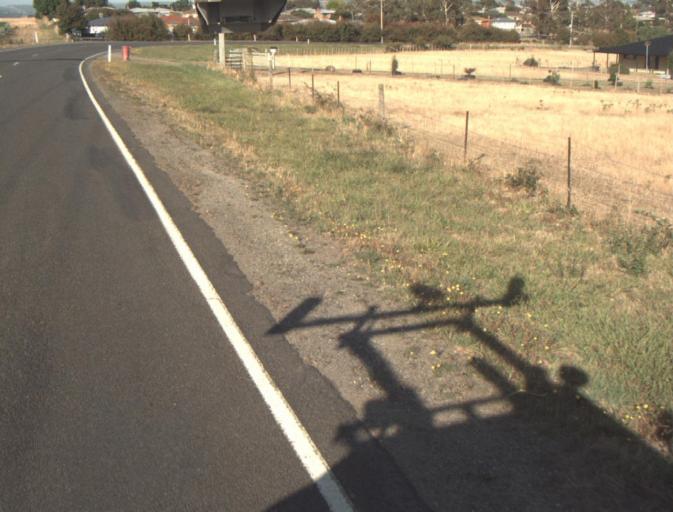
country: AU
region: Tasmania
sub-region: Launceston
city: Newstead
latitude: -41.4363
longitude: 147.1982
